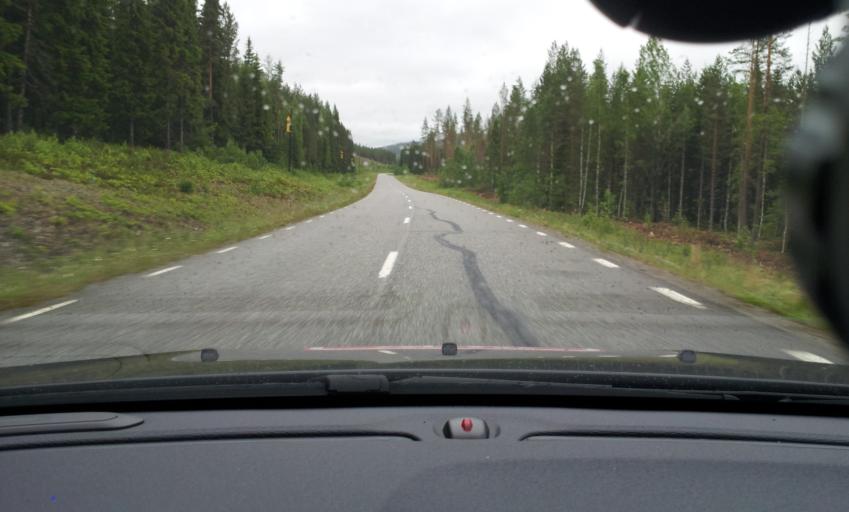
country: SE
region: Jaemtland
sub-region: Ragunda Kommun
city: Hammarstrand
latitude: 63.2772
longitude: 15.8077
